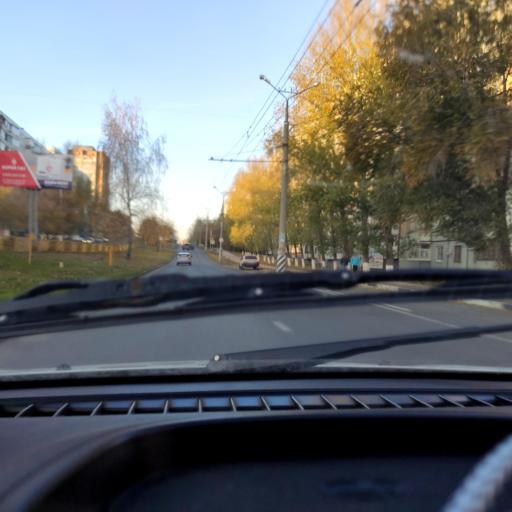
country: RU
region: Samara
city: Zhigulevsk
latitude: 53.4775
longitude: 49.4740
